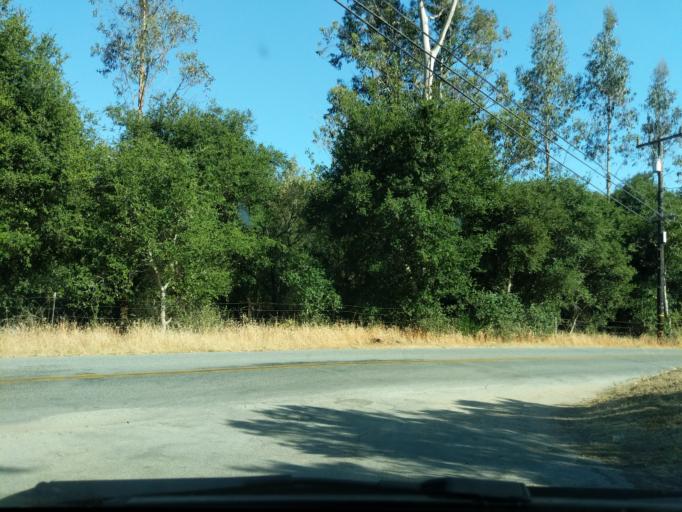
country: US
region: California
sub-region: Monterey County
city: Prunedale
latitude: 36.8000
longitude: -121.6432
